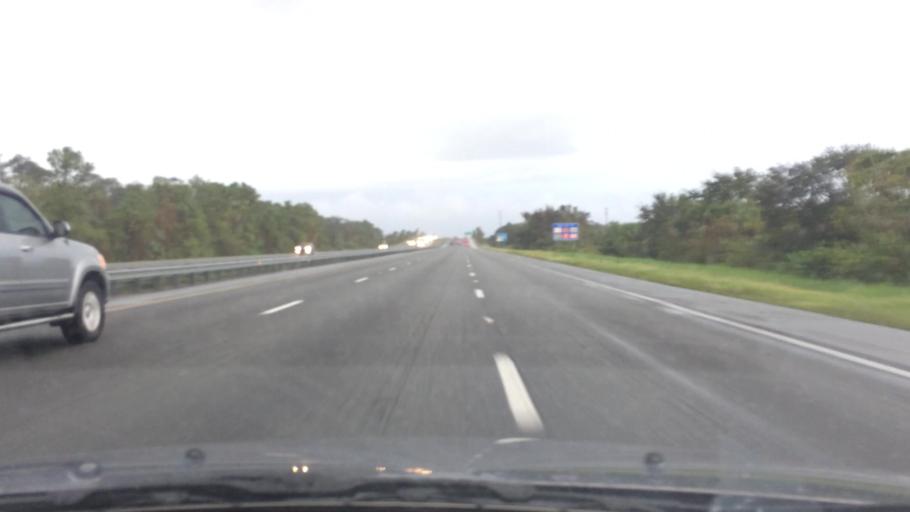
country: US
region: Florida
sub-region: Volusia County
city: Ormond-by-the-Sea
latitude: 29.3264
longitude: -81.1312
